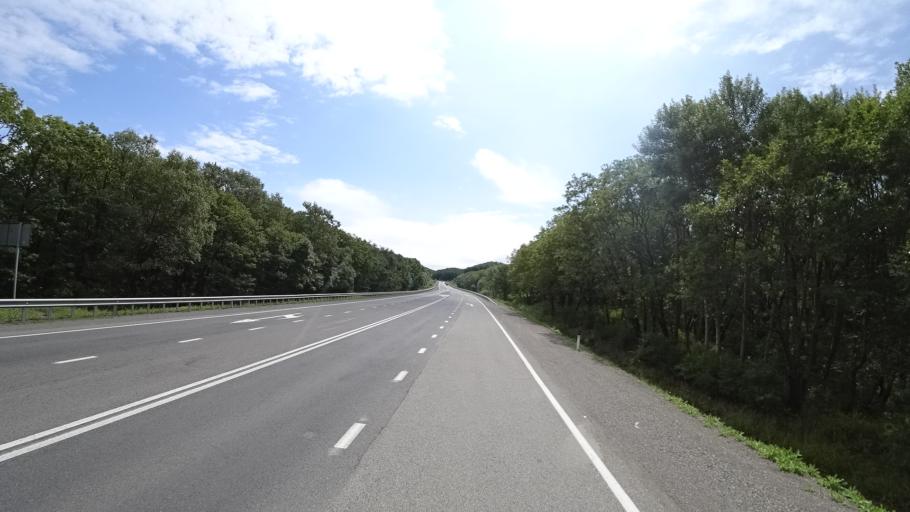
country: RU
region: Primorskiy
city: Lyalichi
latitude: 44.1384
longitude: 132.4287
